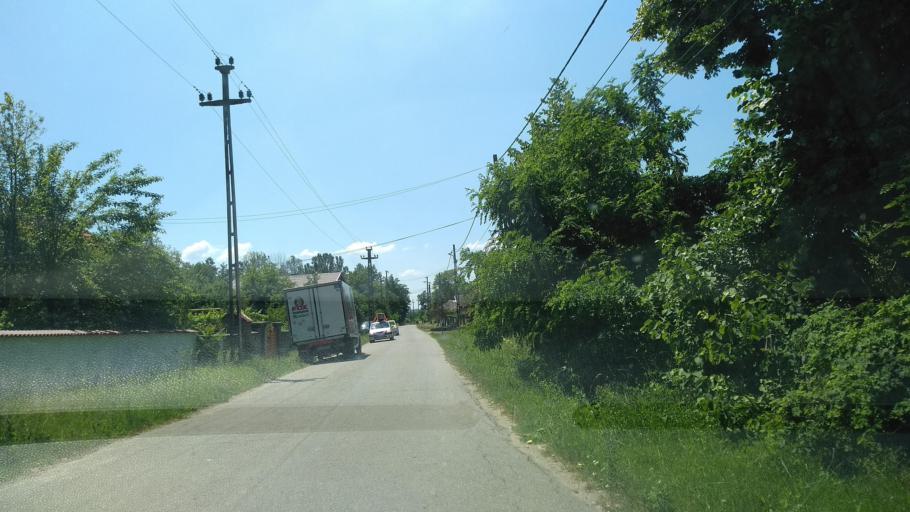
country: RO
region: Gorj
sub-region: Comuna Turcinesti
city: Turcinesti
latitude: 45.1139
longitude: 23.3161
